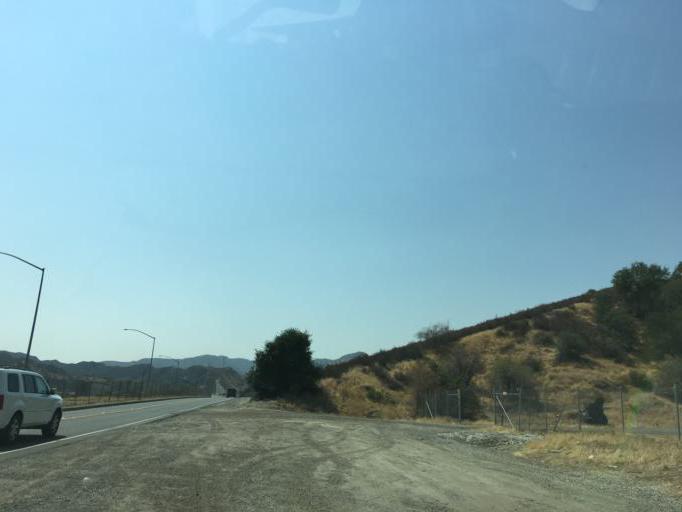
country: US
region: California
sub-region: Los Angeles County
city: Santa Clarita
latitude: 34.3705
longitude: -118.5608
